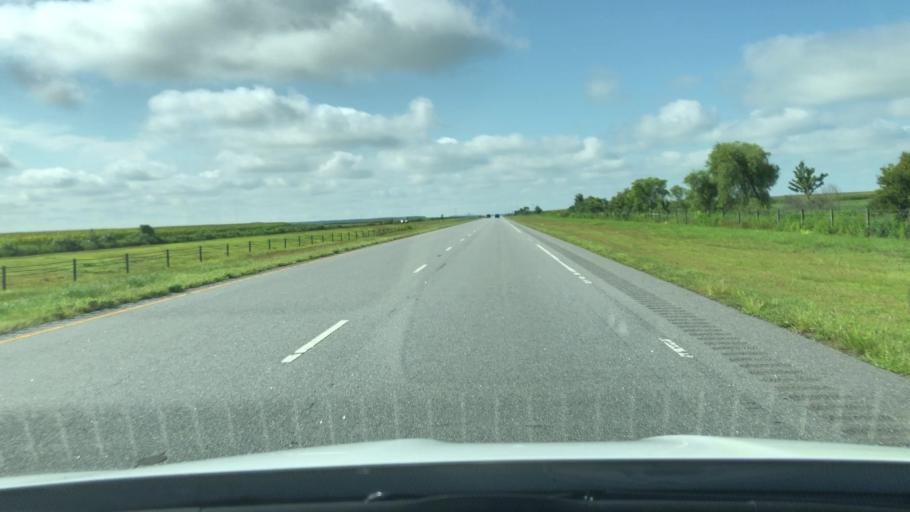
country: US
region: North Carolina
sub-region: Pasquotank County
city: Elizabeth City
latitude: 36.3500
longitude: -76.3143
